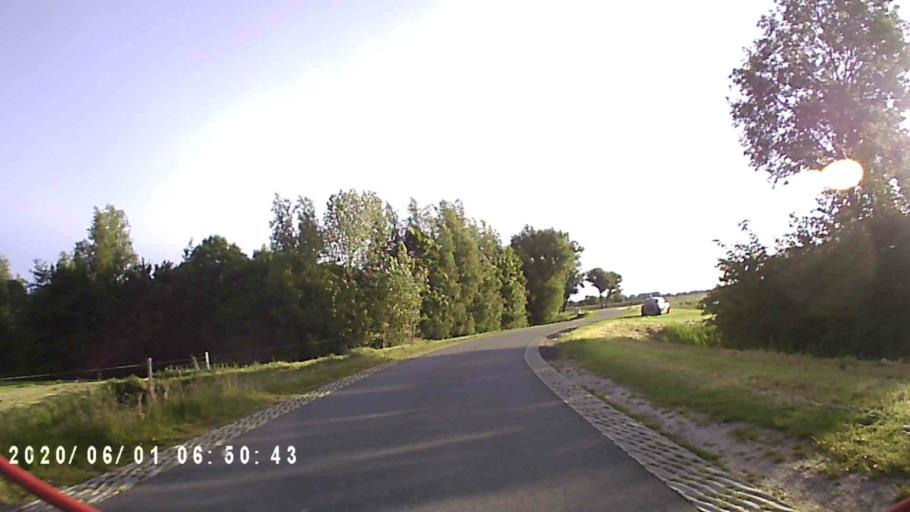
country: NL
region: Friesland
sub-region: Gemeente Kollumerland en Nieuwkruisland
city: Kollum
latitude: 53.3031
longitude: 6.1306
